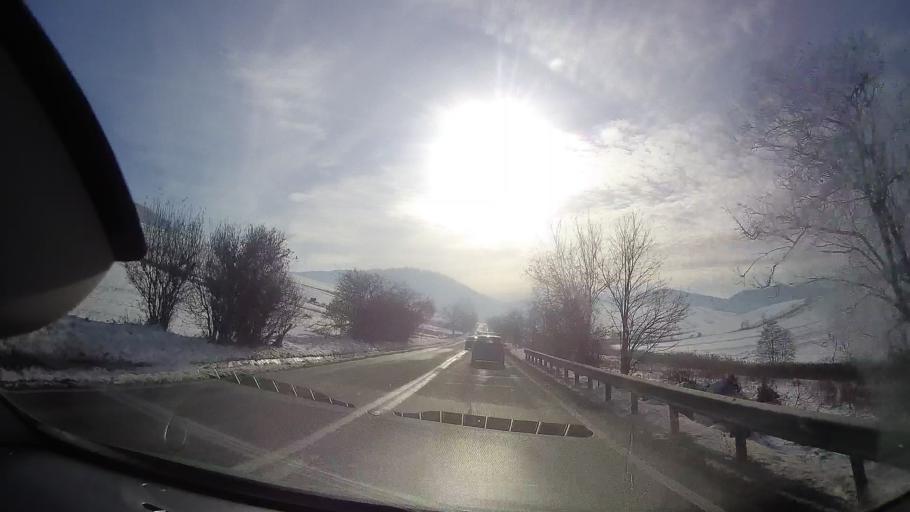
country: RO
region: Neamt
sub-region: Comuna Garcina
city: Garcina
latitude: 46.9876
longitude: 26.3605
